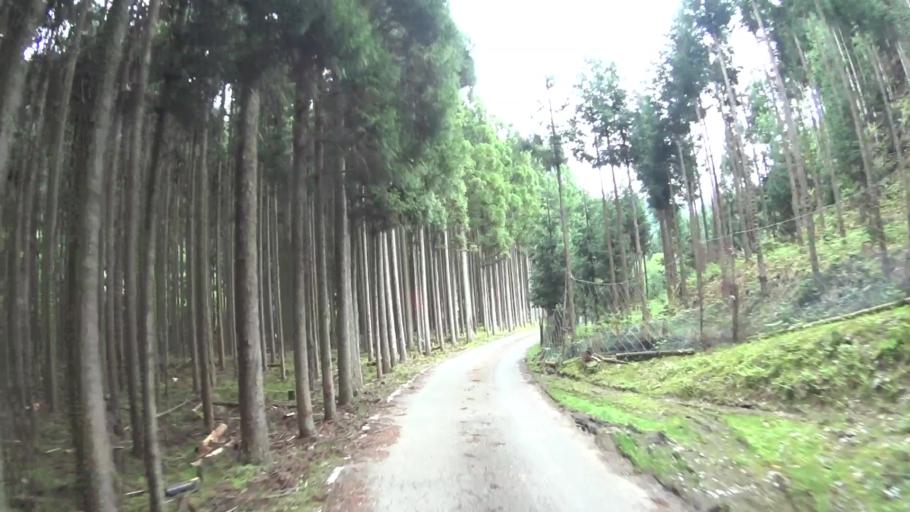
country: JP
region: Kyoto
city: Kameoka
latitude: 35.1123
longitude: 135.6326
